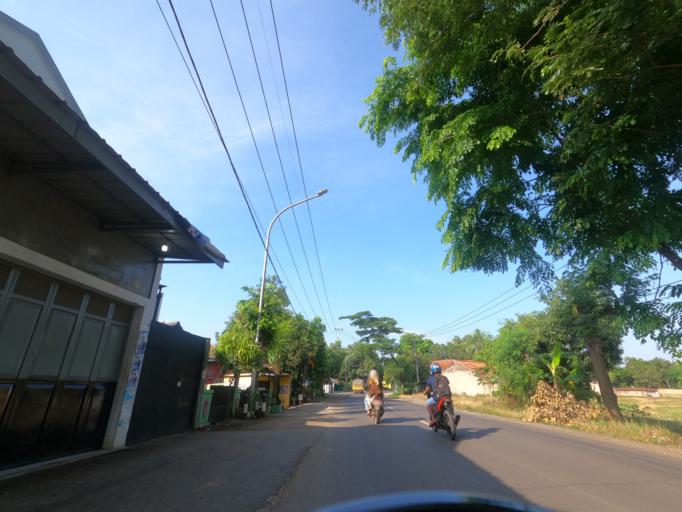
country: ID
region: West Java
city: Pamanukan
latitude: -6.5542
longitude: 107.8270
